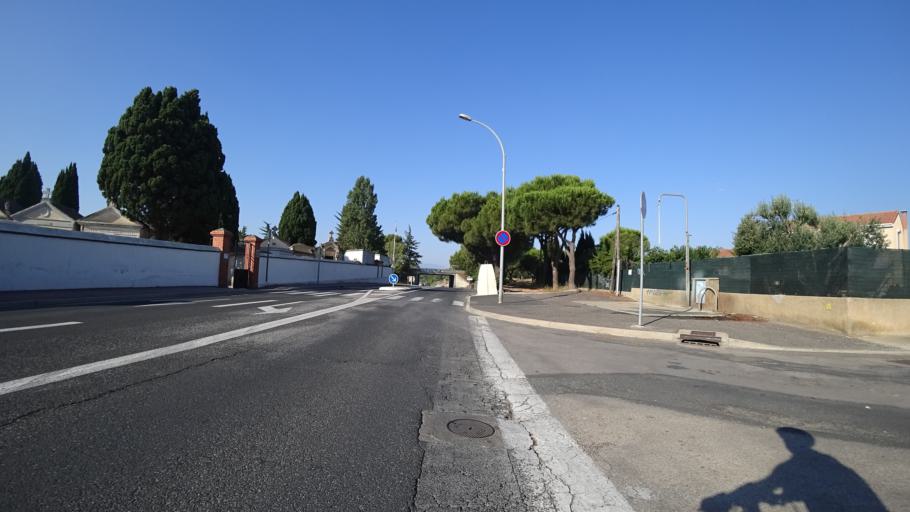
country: FR
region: Languedoc-Roussillon
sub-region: Departement des Pyrenees-Orientales
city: Canet-en-Roussillon
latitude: 42.7036
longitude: 3.0036
